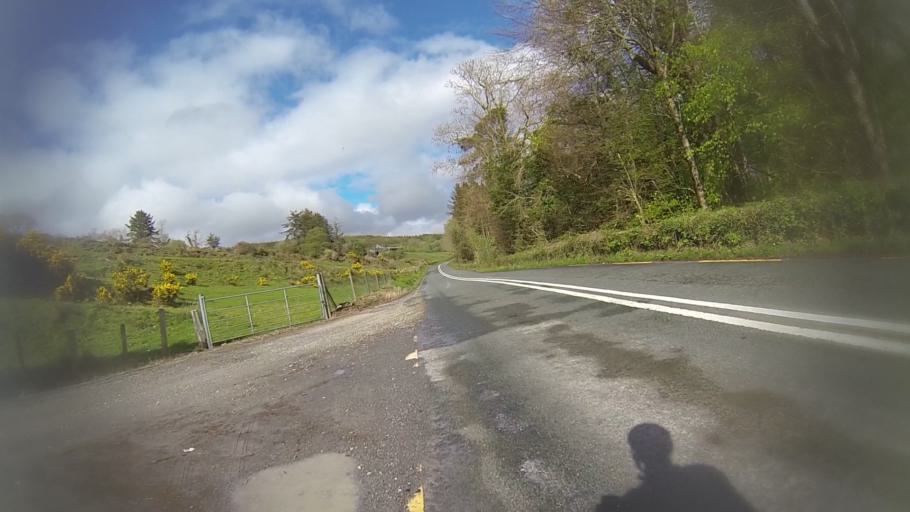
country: IE
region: Munster
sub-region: Ciarrai
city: Kenmare
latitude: 51.8552
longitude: -9.7314
